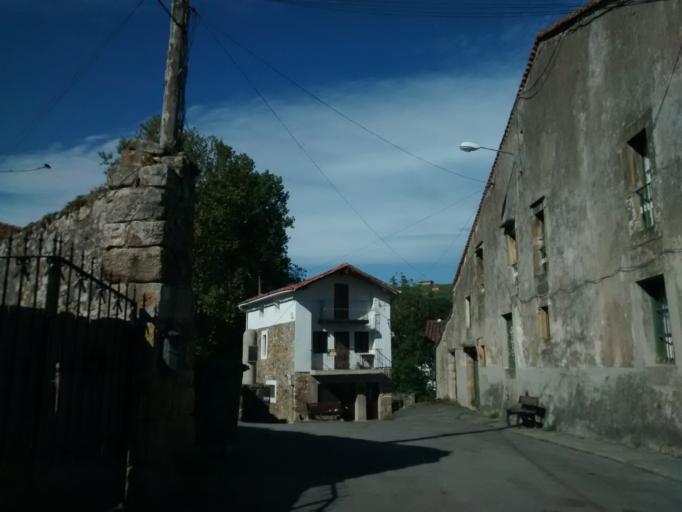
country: ES
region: Cantabria
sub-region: Provincia de Cantabria
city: Lierganes
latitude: 43.3438
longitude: -3.7459
